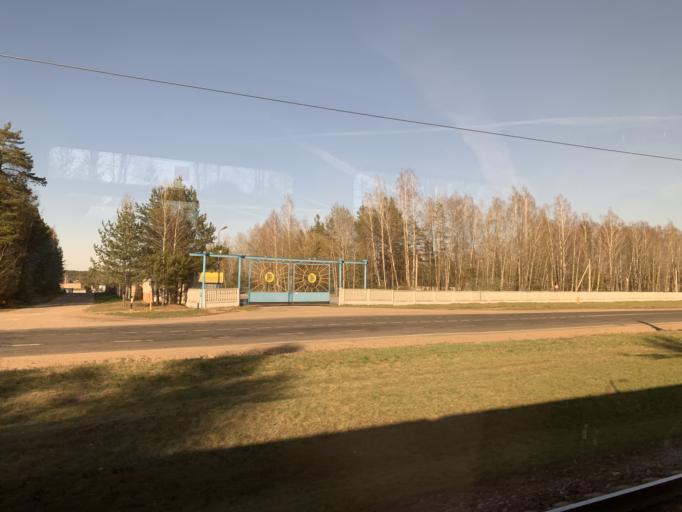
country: BY
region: Grodnenskaya
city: Smarhon'
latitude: 54.4402
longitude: 26.5050
